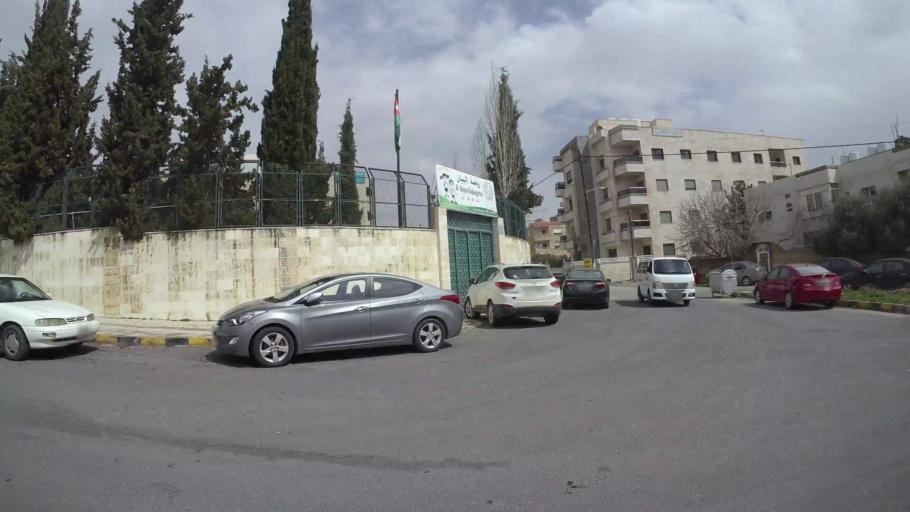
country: JO
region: Amman
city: Umm as Summaq
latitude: 31.8991
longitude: 35.8409
